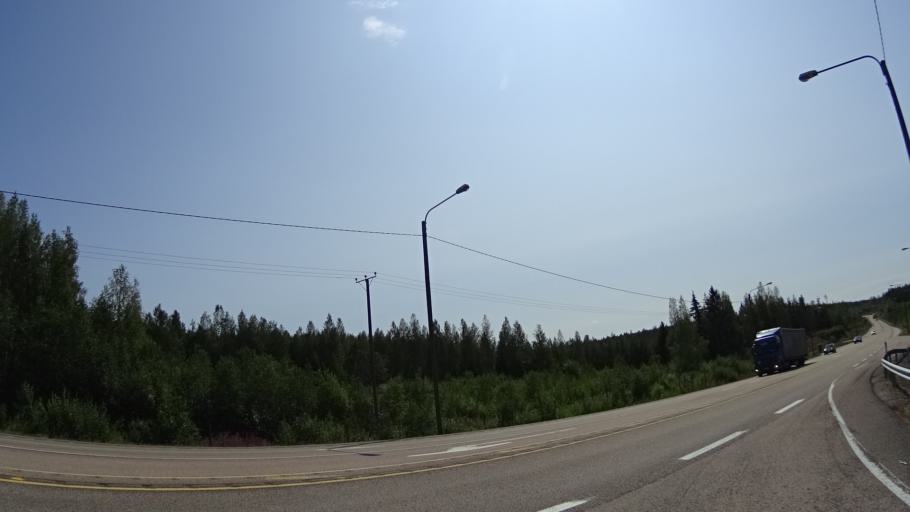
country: FI
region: Central Finland
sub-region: Jaemsae
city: Jaemsae
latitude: 61.7769
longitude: 24.8928
